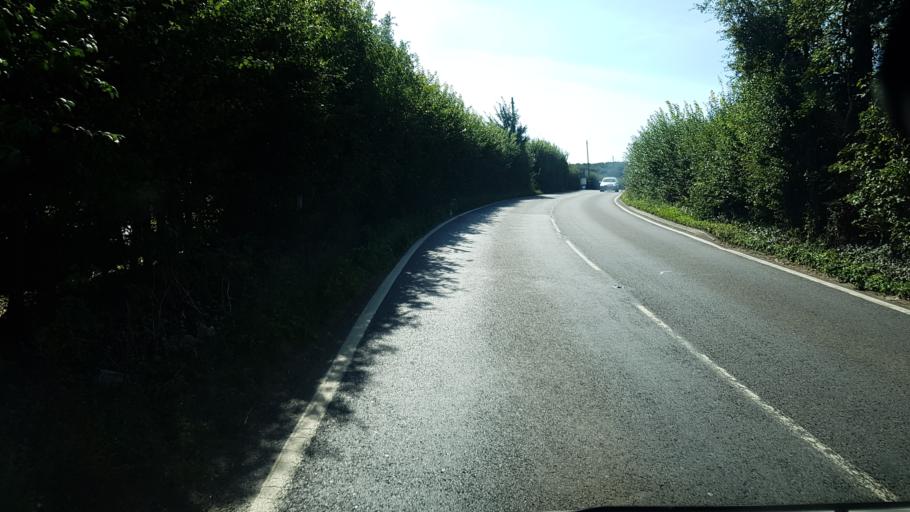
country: GB
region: England
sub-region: Kent
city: Borough Green
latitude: 51.2877
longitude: 0.3500
